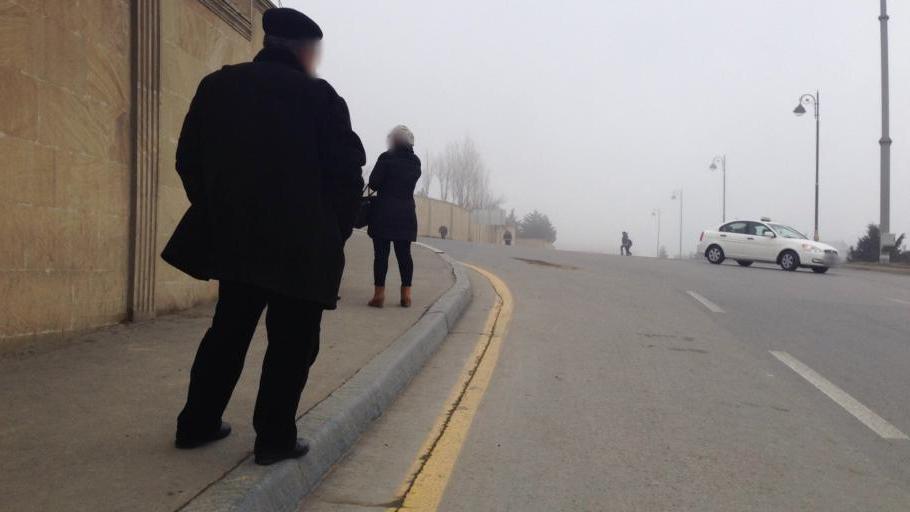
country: AZ
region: Baki
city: Qaracuxur
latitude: 40.3503
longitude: 49.9603
